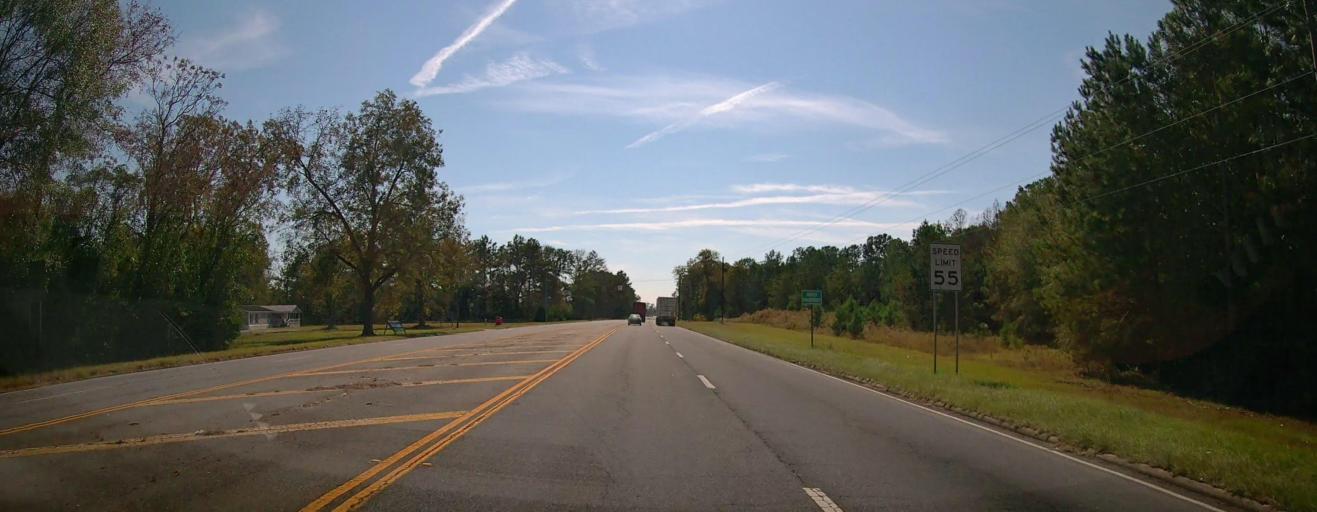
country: US
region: Georgia
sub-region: Lee County
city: Leesburg
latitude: 31.7846
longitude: -83.9643
